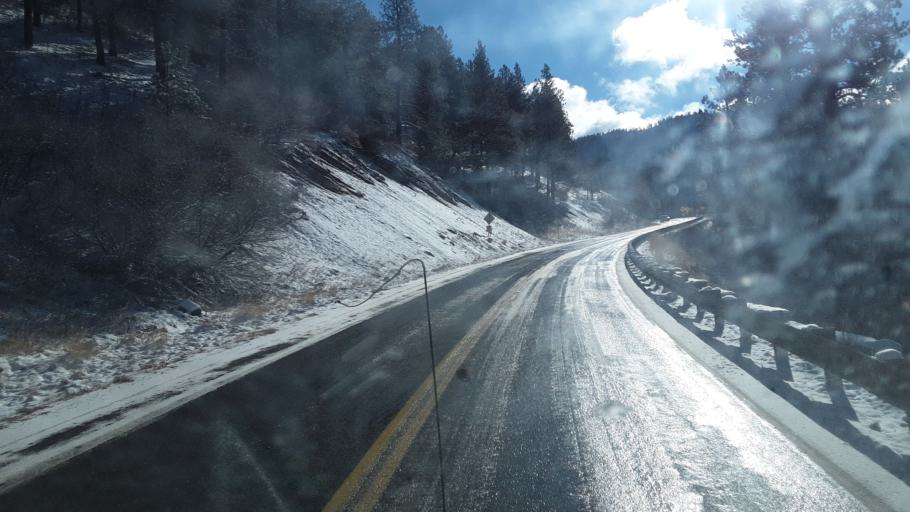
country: US
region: Colorado
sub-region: La Plata County
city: Durango
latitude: 37.3326
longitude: -107.7389
